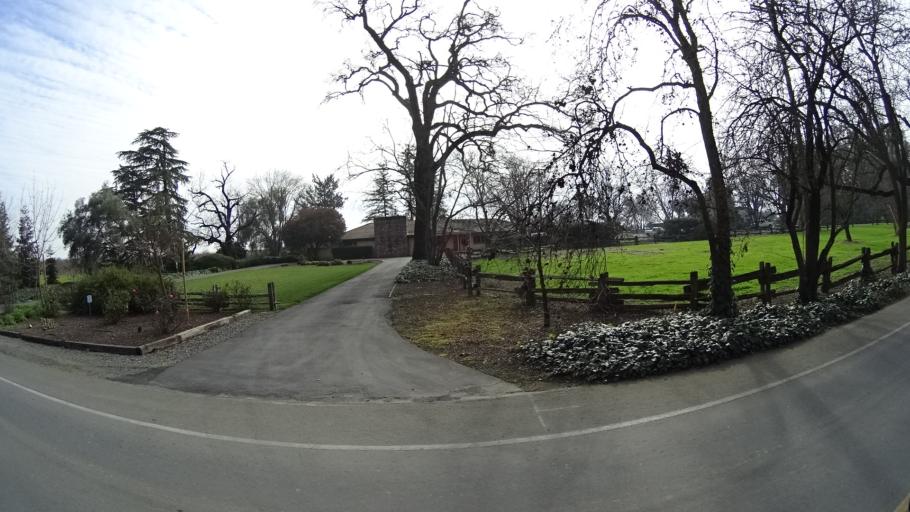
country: US
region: California
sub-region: Yolo County
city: Davis
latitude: 38.5389
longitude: -121.7104
